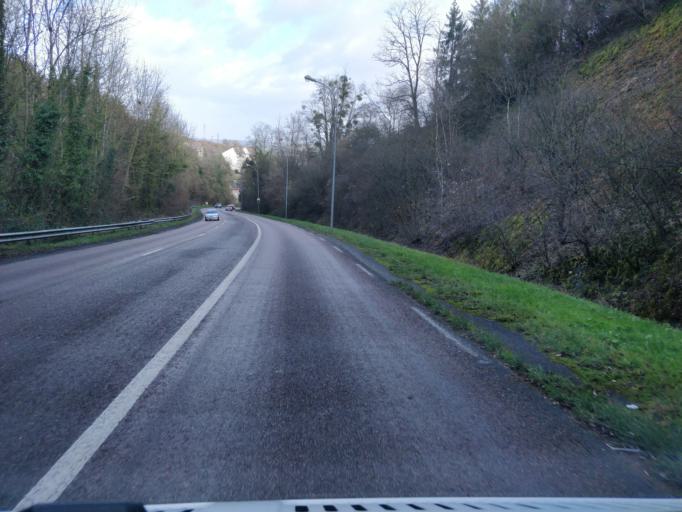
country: FR
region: Bourgogne
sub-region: Departement de l'Yonne
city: Paron
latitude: 48.1925
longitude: 3.2549
